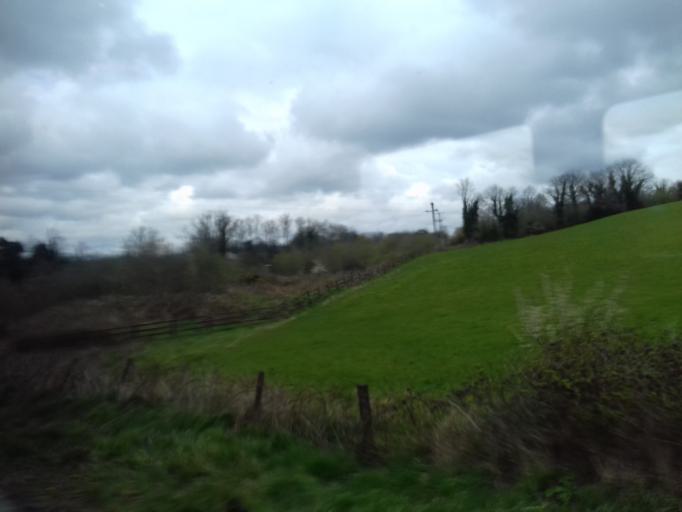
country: IE
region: Leinster
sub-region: An Longfort
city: Longford
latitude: 53.8553
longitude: -7.9131
